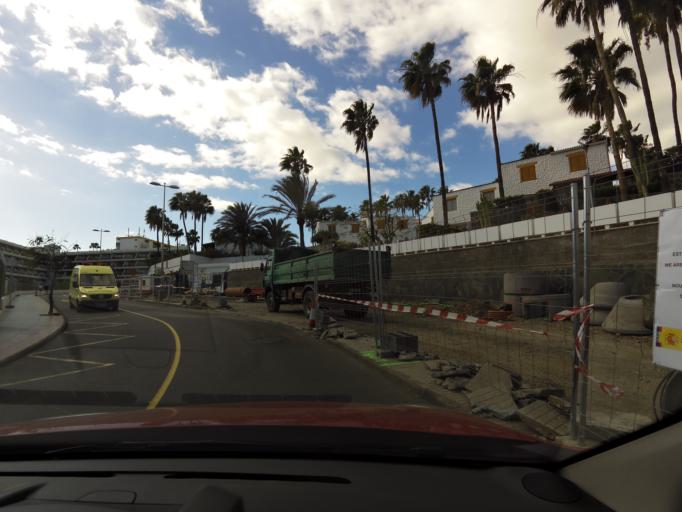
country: ES
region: Canary Islands
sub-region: Provincia de Las Palmas
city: Playa del Ingles
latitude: 27.7585
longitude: -15.5726
